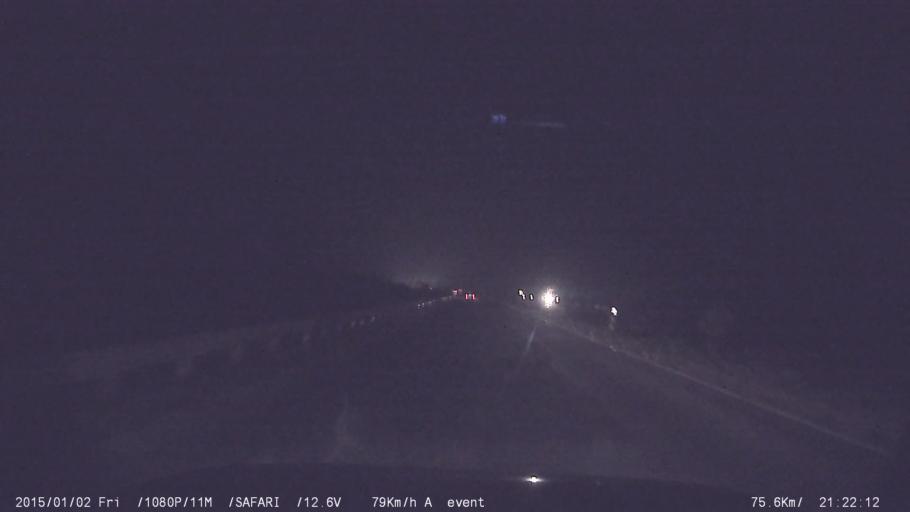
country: IN
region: Tamil Nadu
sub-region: Kancheepuram
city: Kanchipuram
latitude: 12.8932
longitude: 79.5875
